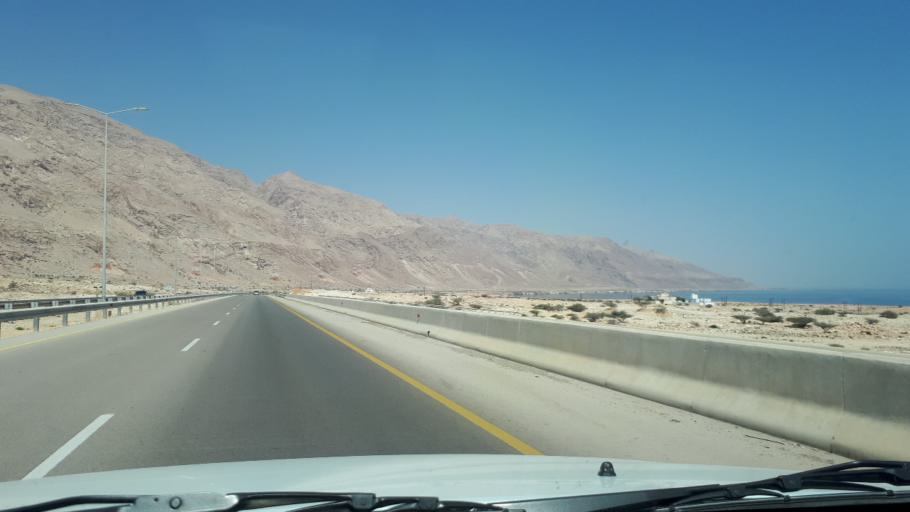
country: OM
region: Ash Sharqiyah
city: Sur
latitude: 22.7467
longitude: 59.3211
